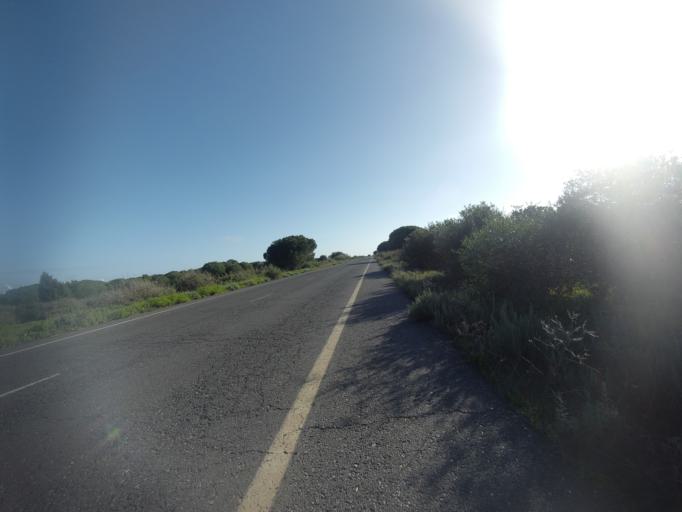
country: ES
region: Andalusia
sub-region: Provincia de Huelva
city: Huelva
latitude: 37.2352
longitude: -6.9648
